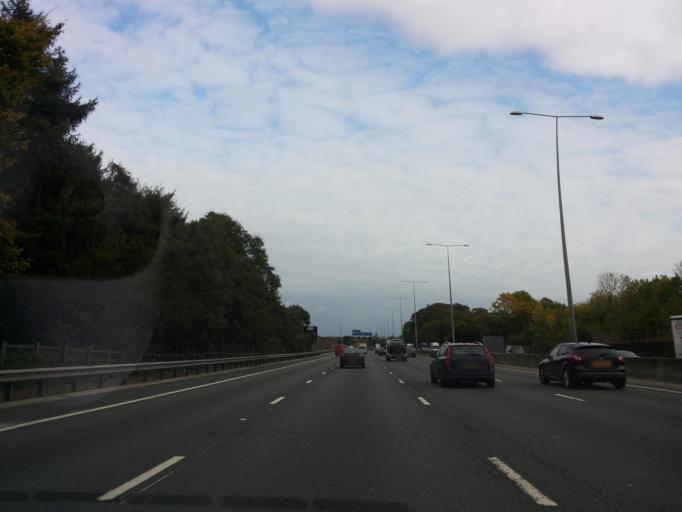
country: GB
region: England
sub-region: Hertfordshire
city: Chorleywood
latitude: 51.6727
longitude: -0.4747
